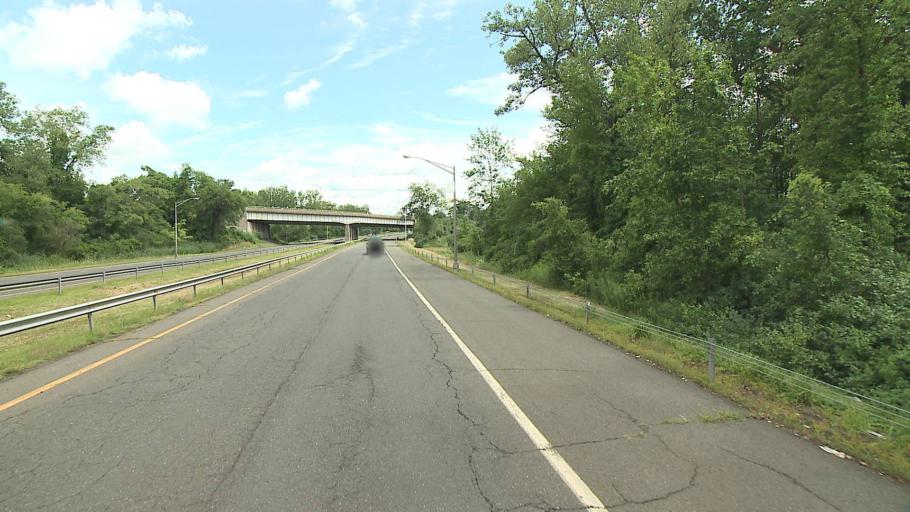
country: US
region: Connecticut
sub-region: Hartford County
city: Kensington
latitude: 41.6466
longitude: -72.7682
